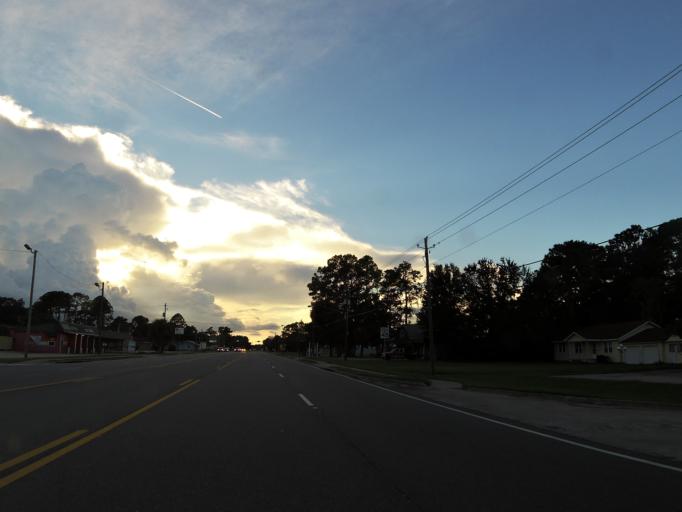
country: US
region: Georgia
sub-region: Camden County
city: St Marys
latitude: 30.7450
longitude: -81.5588
